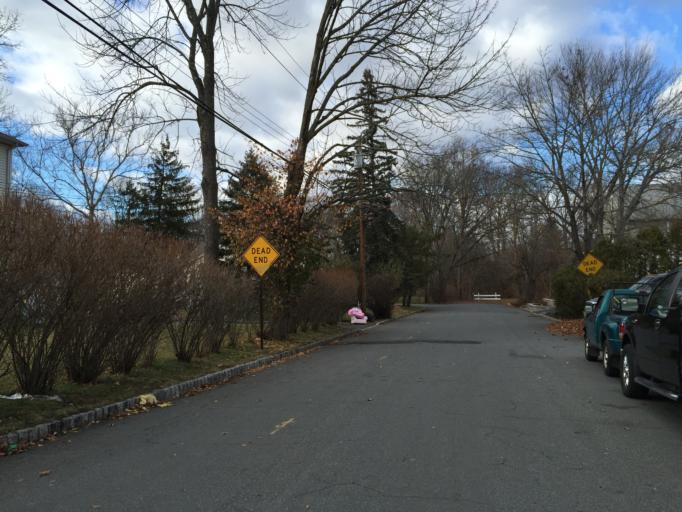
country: US
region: New Jersey
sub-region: Union County
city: New Providence
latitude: 40.7007
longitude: -74.4004
